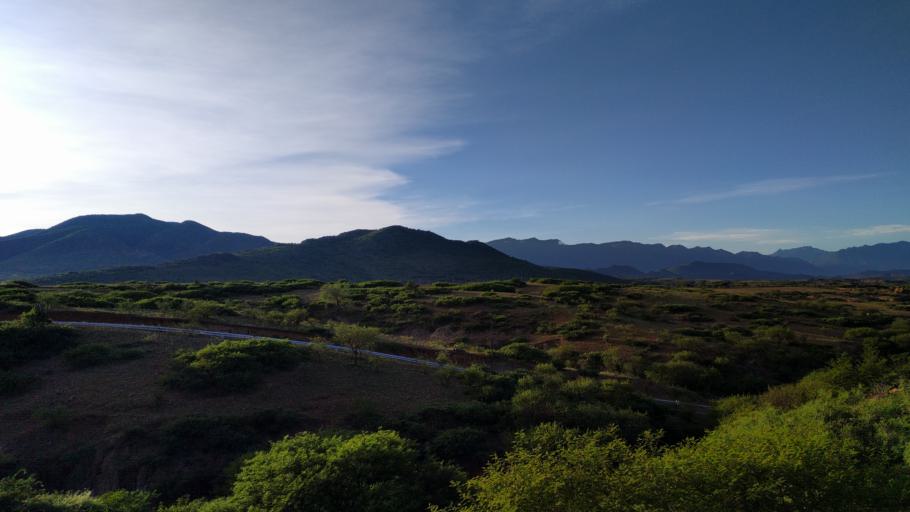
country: BO
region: Tarija
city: Tarija
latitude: -21.5214
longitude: -64.5654
